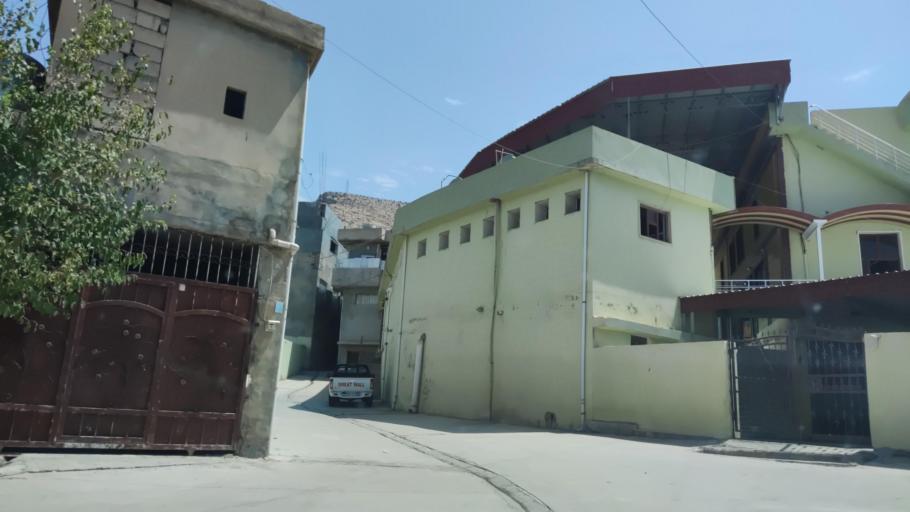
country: IQ
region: Arbil
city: Shaqlawah
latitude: 36.5506
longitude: 44.3535
